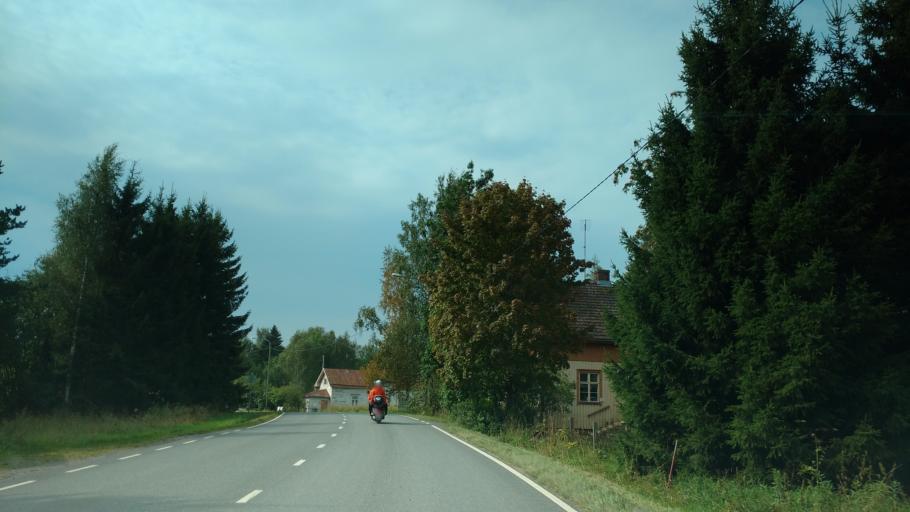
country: FI
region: Varsinais-Suomi
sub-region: Loimaa
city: Koski Tl
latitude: 60.6618
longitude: 23.1491
